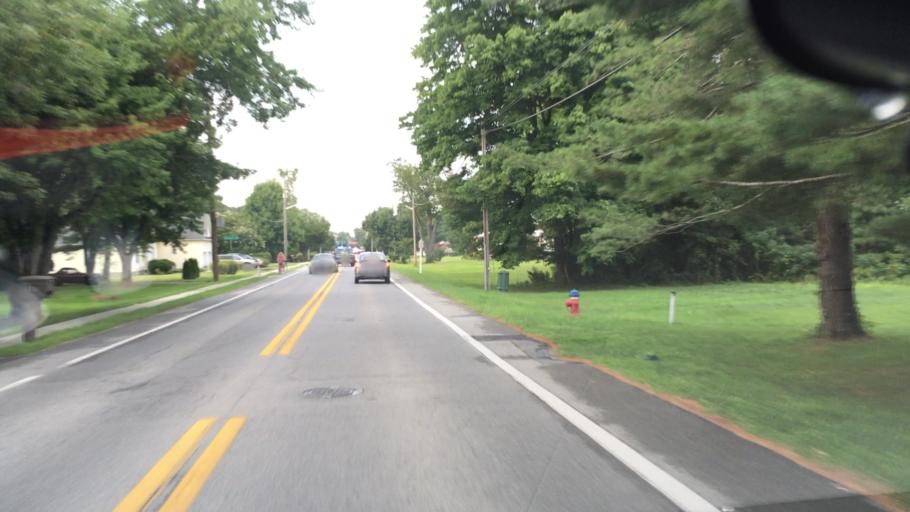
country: US
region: Delaware
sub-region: Sussex County
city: Ocean View
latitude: 38.5389
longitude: -75.0910
